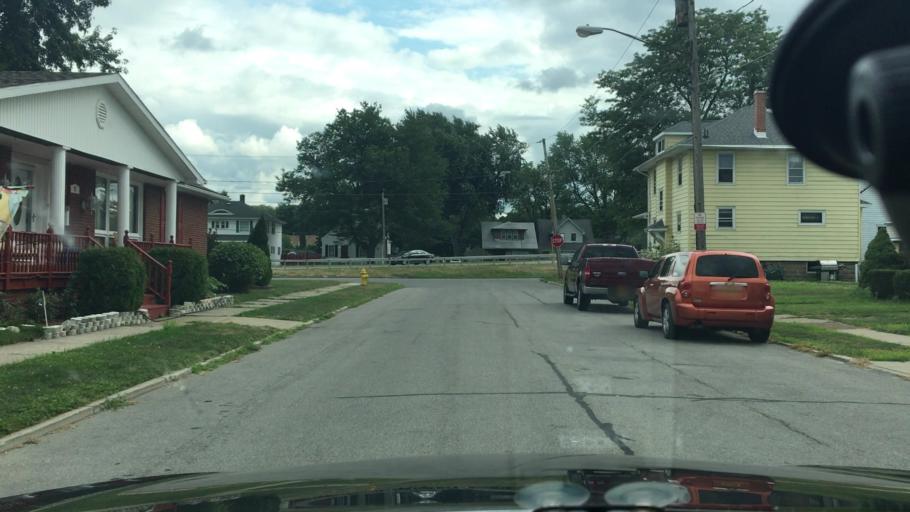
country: US
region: New York
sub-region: Erie County
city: Lackawanna
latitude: 42.8305
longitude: -78.8187
